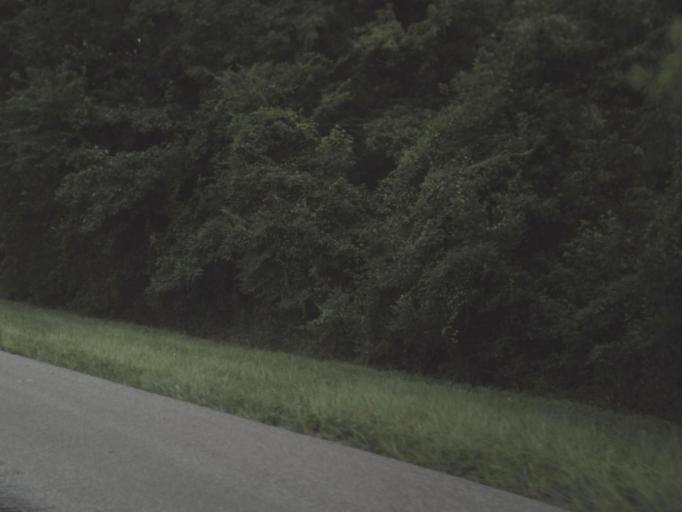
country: US
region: Florida
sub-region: Hernando County
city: Hill 'n Dale
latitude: 28.4582
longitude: -82.2759
